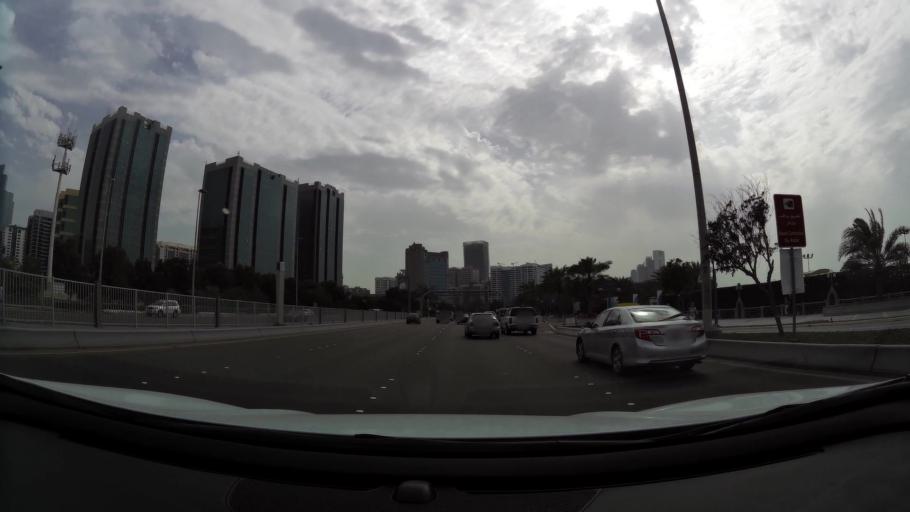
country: AE
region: Abu Dhabi
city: Abu Dhabi
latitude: 24.4780
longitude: 54.3452
